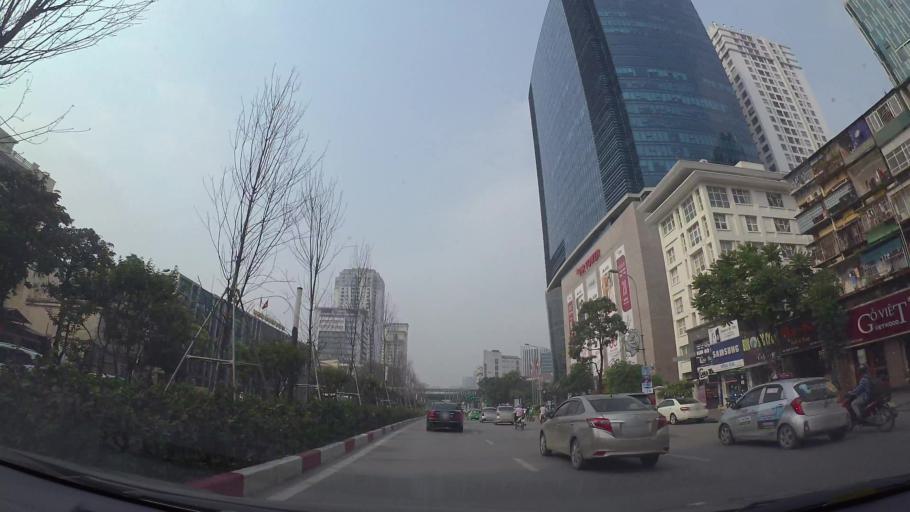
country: VN
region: Ha Noi
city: Cau Giay
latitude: 21.0239
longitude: 105.8105
